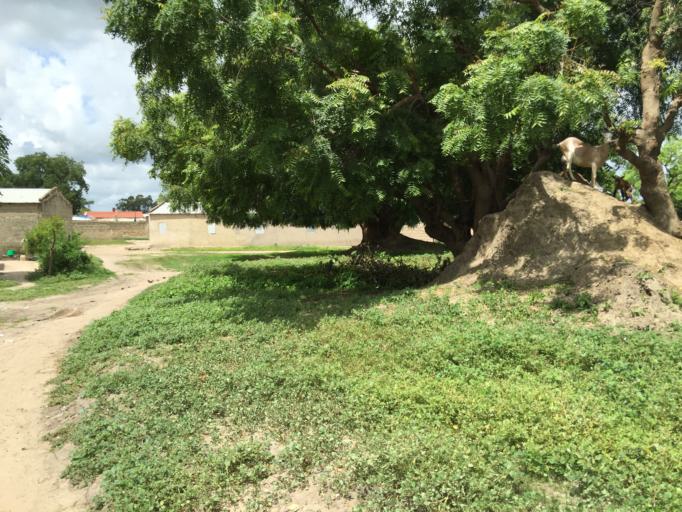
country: SN
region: Fatick
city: Sokone
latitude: 13.7829
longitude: -16.4716
